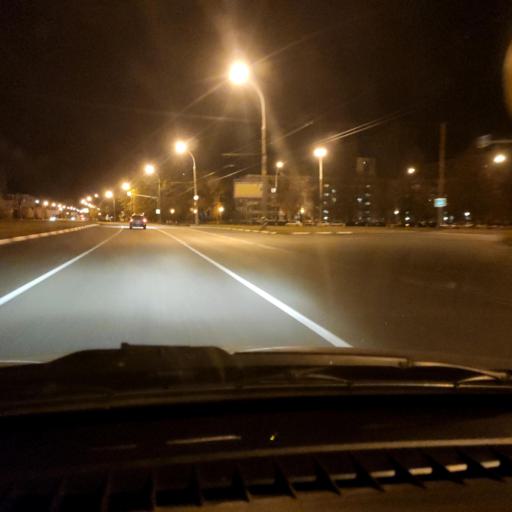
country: RU
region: Samara
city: Tol'yatti
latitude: 53.5191
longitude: 49.2943
